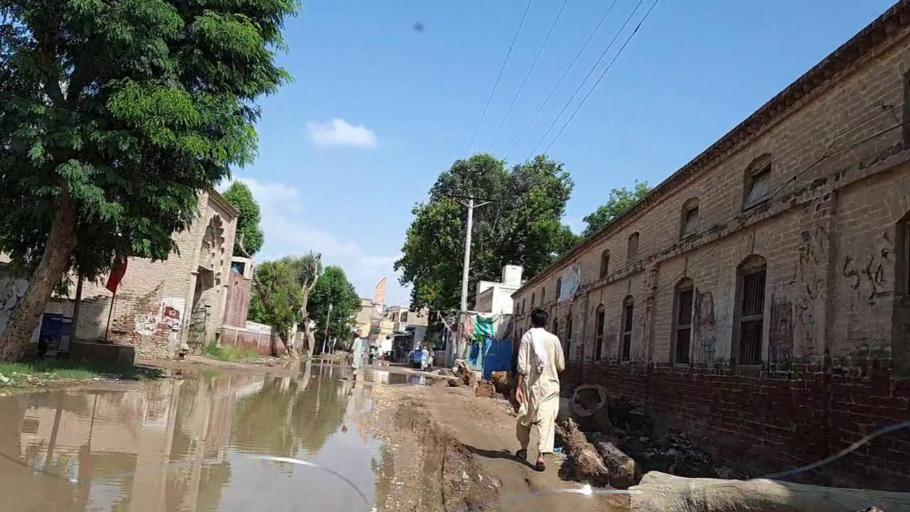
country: PK
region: Sindh
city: Pad Idan
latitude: 26.7750
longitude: 68.2985
